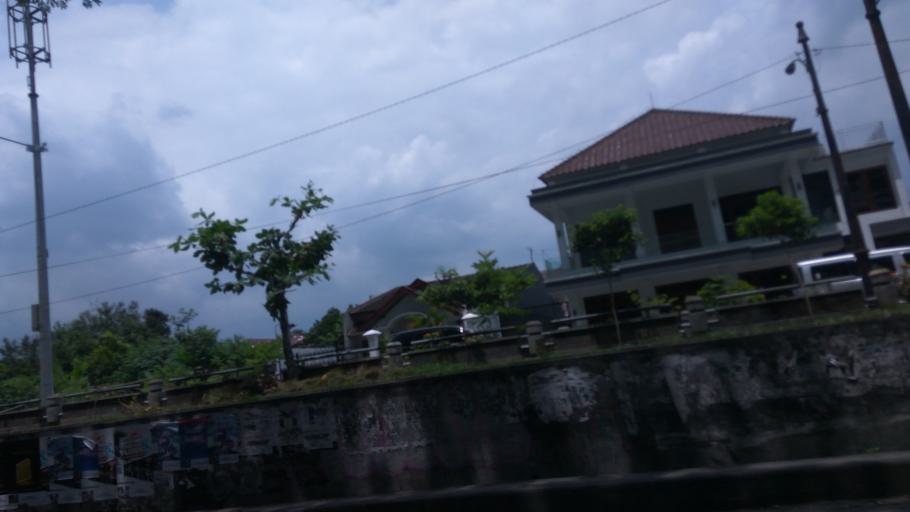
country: ID
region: Daerah Istimewa Yogyakarta
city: Yogyakarta
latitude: -7.7670
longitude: 110.3847
